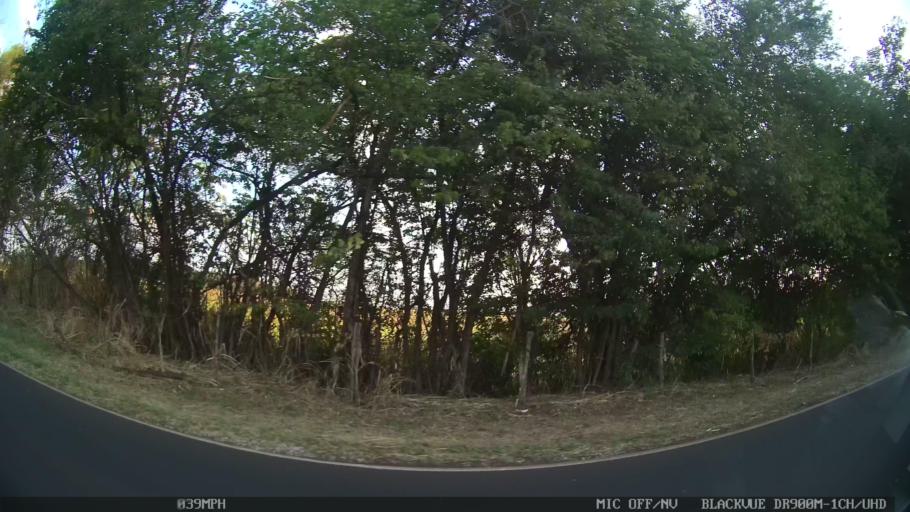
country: BR
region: Sao Paulo
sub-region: Ribeirao Preto
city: Ribeirao Preto
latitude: -21.1554
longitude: -47.7766
